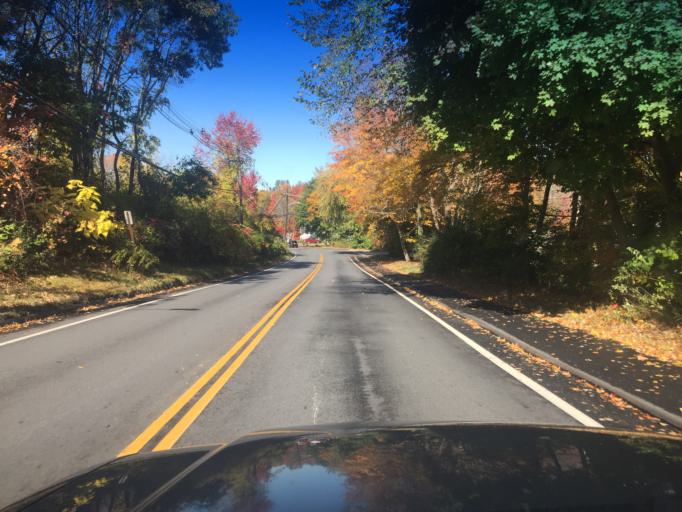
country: US
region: Massachusetts
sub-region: Middlesex County
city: Hudson
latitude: 42.3852
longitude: -71.5491
